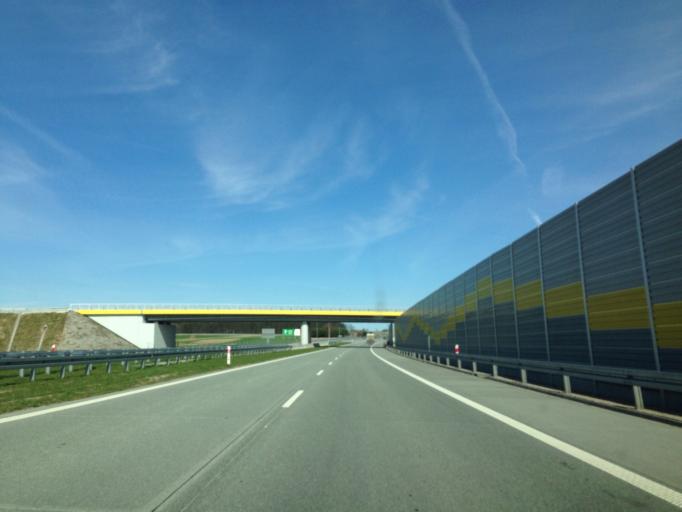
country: PL
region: Lodz Voivodeship
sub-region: Powiat sieradzki
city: Sieradz
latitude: 51.5890
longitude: 18.8113
